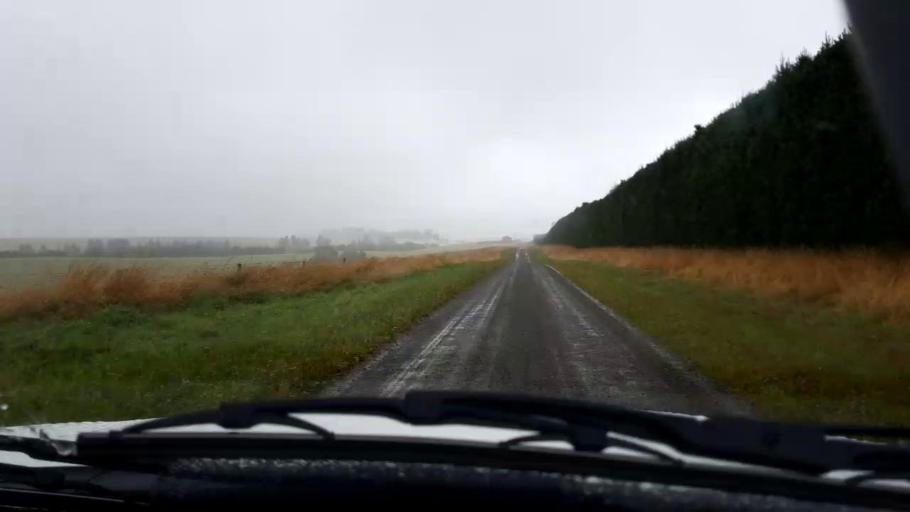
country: NZ
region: Canterbury
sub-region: Timaru District
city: Pleasant Point
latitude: -44.1691
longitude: 171.1532
